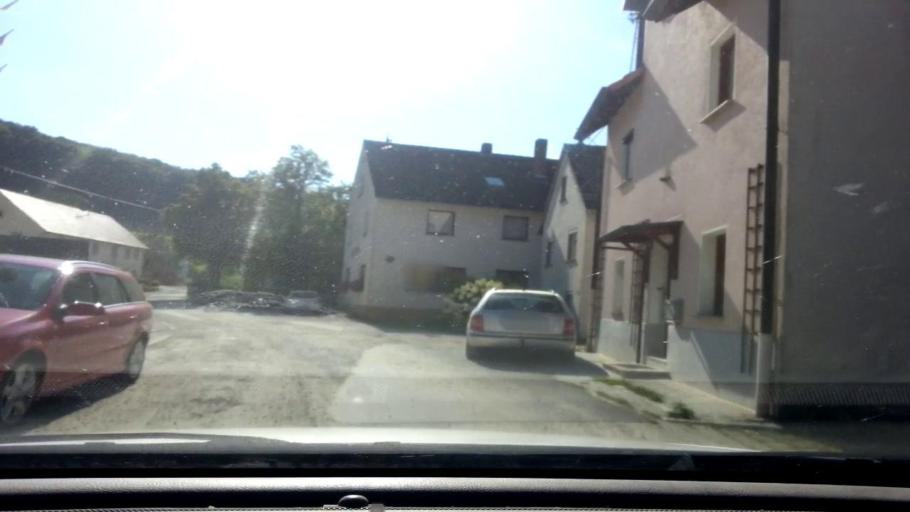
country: DE
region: Bavaria
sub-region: Upper Franconia
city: Schesslitz
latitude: 49.9959
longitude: 11.0801
